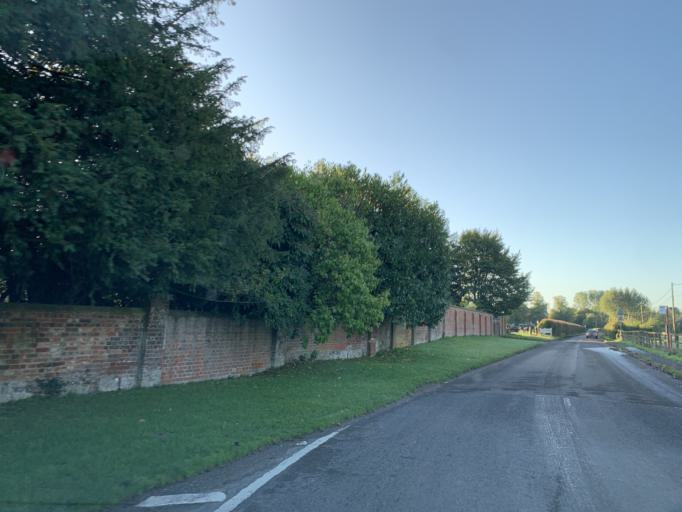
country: GB
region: England
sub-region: Wiltshire
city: Woodford
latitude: 51.0954
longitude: -1.8163
